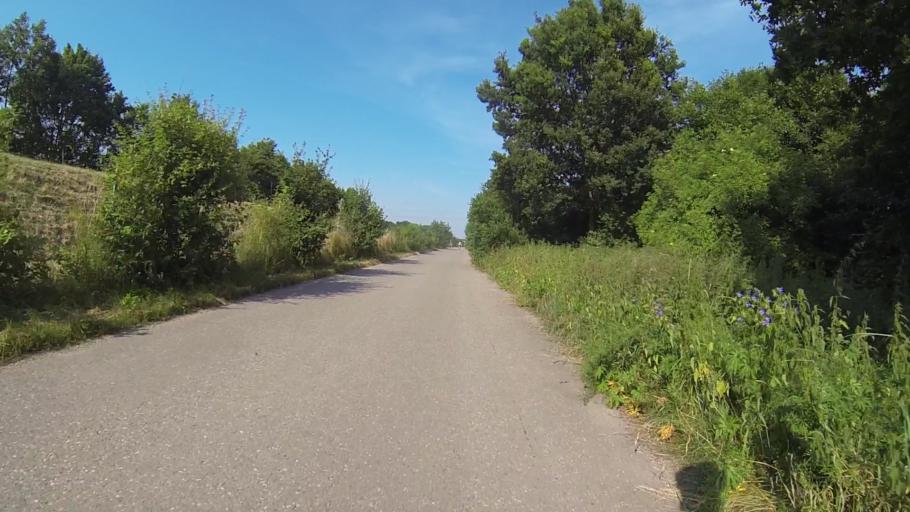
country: DE
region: Bavaria
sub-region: Swabia
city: Neu-Ulm
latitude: 48.3896
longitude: 10.0477
